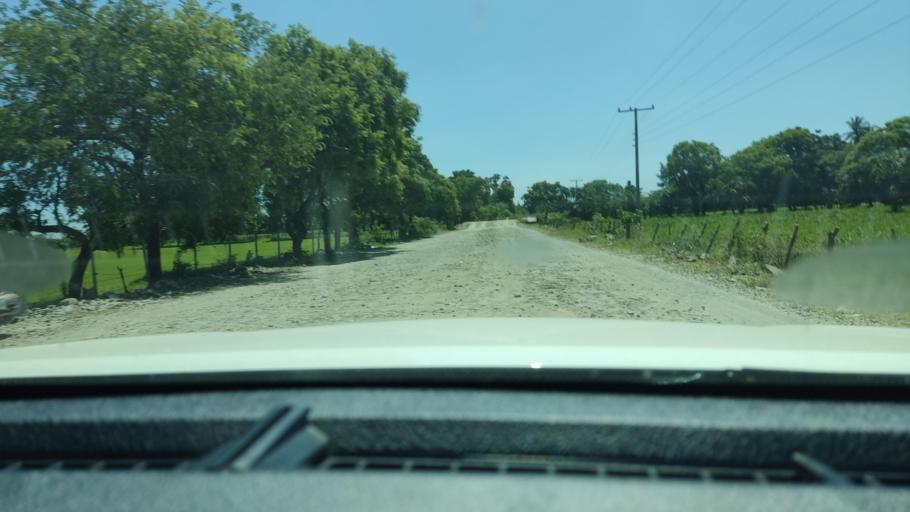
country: SV
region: Ahuachapan
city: San Francisco Menendez
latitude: 13.7529
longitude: -90.1260
